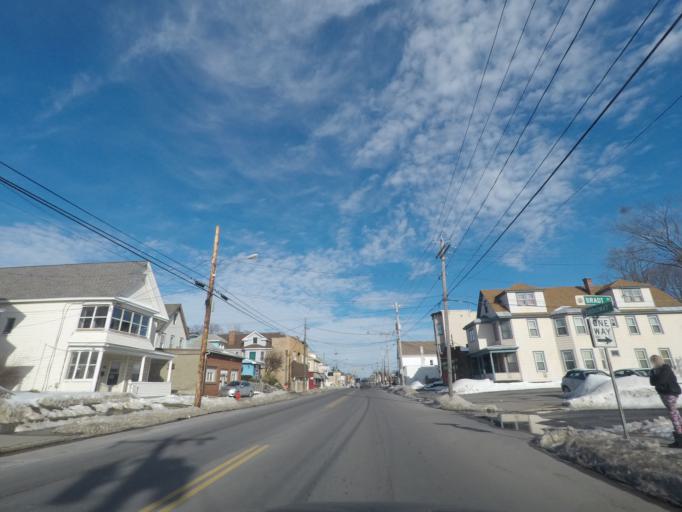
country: US
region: New York
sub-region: Schenectady County
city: Rotterdam
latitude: 42.7972
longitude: -73.9668
